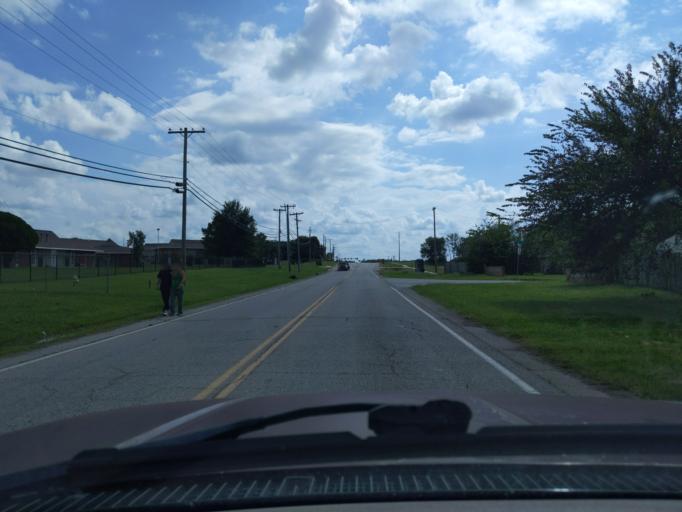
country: US
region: Oklahoma
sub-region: Tulsa County
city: Oakhurst
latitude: 36.0793
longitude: -96.0117
